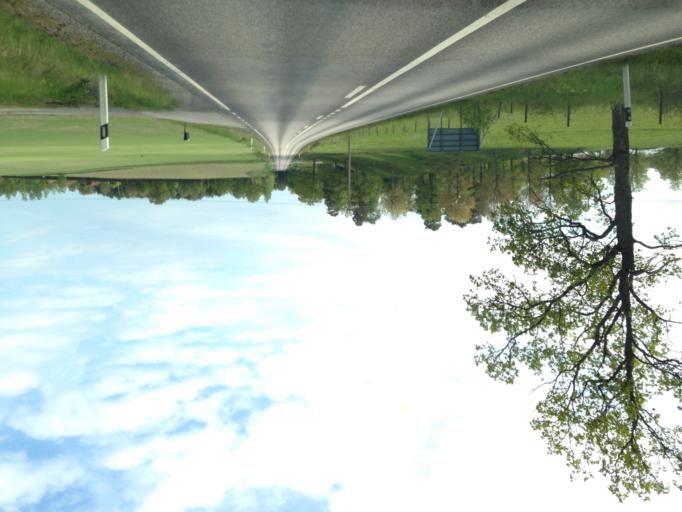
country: SE
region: Soedermanland
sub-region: Flens Kommun
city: Malmkoping
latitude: 58.9966
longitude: 16.8441
